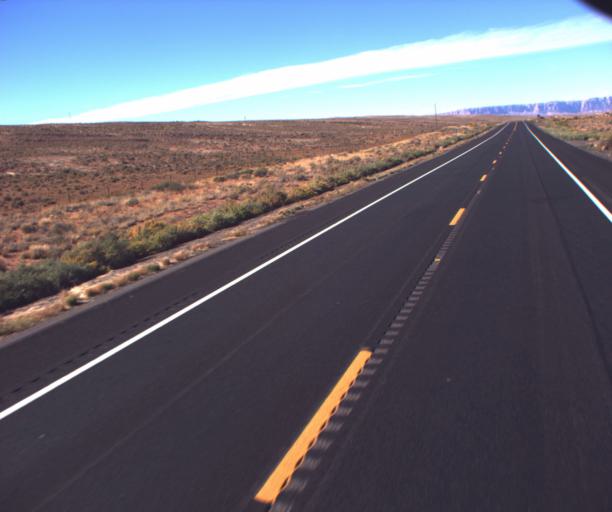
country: US
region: Arizona
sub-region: Coconino County
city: LeChee
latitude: 36.5455
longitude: -111.6215
